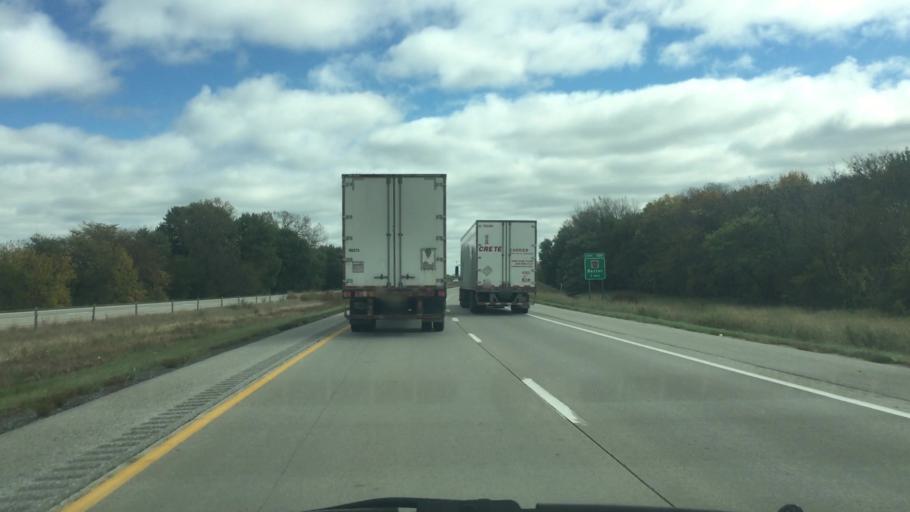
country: US
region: Iowa
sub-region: Jasper County
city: Colfax
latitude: 41.6990
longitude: -93.2023
